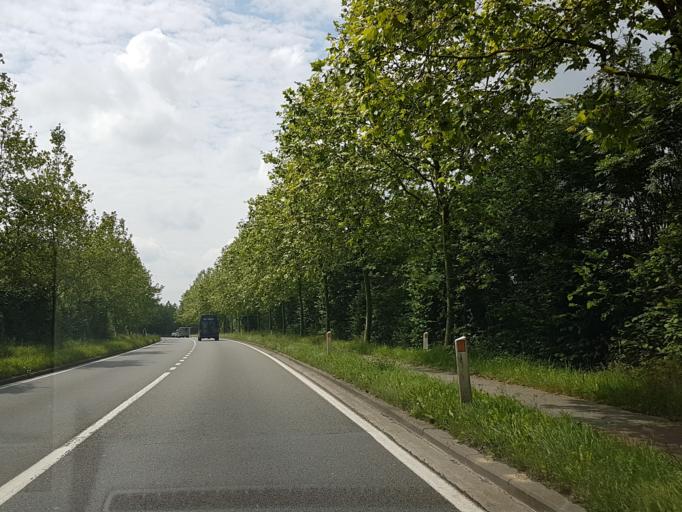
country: BE
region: Flanders
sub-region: Provincie Vlaams-Brabant
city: Liedekerke
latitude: 50.8886
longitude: 4.1153
